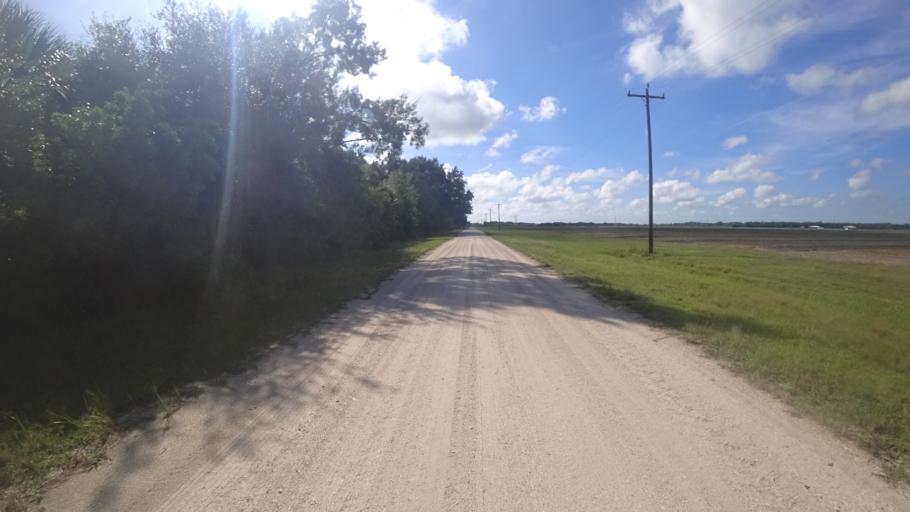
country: US
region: Florida
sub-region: Hillsborough County
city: Ruskin
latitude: 27.6299
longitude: -82.4972
